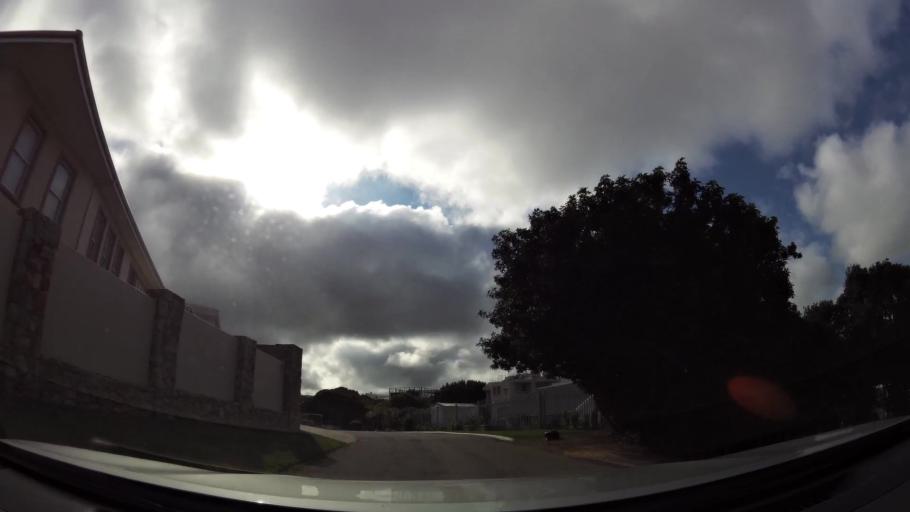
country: ZA
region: Western Cape
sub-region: Eden District Municipality
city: Plettenberg Bay
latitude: -34.0719
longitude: 23.3716
